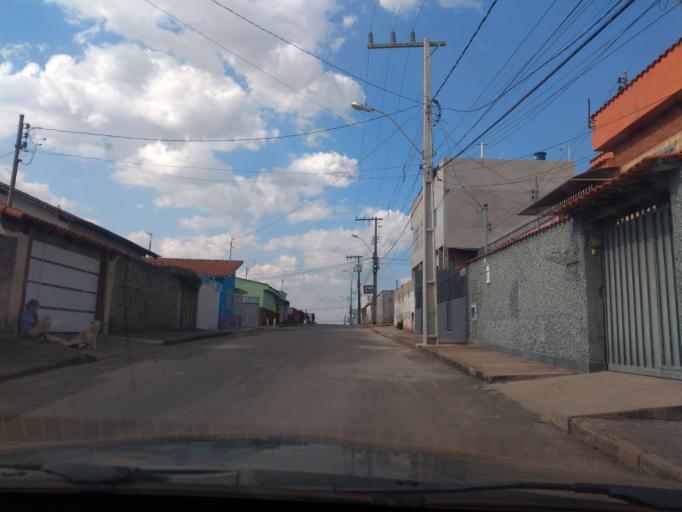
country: BR
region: Minas Gerais
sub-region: Tres Coracoes
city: Tres Coracoes
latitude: -21.6930
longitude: -45.2414
